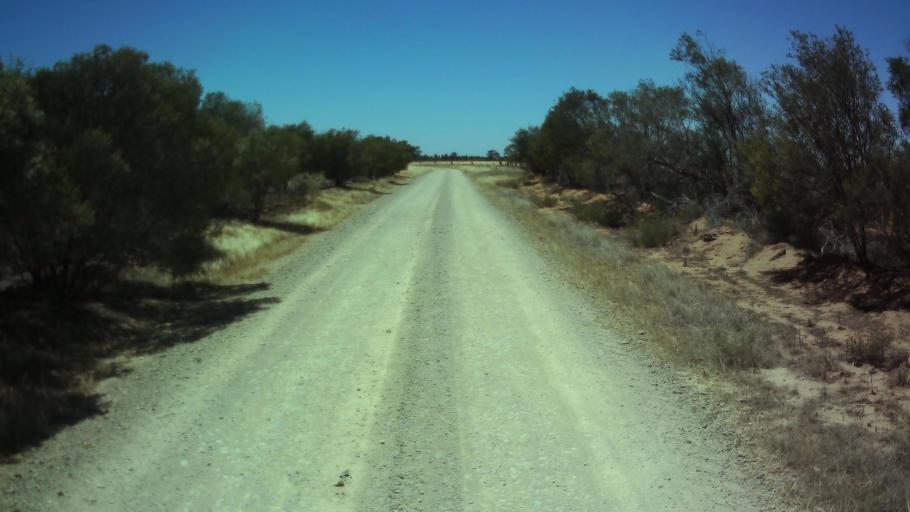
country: AU
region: New South Wales
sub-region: Weddin
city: Grenfell
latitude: -34.0419
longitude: 147.7933
